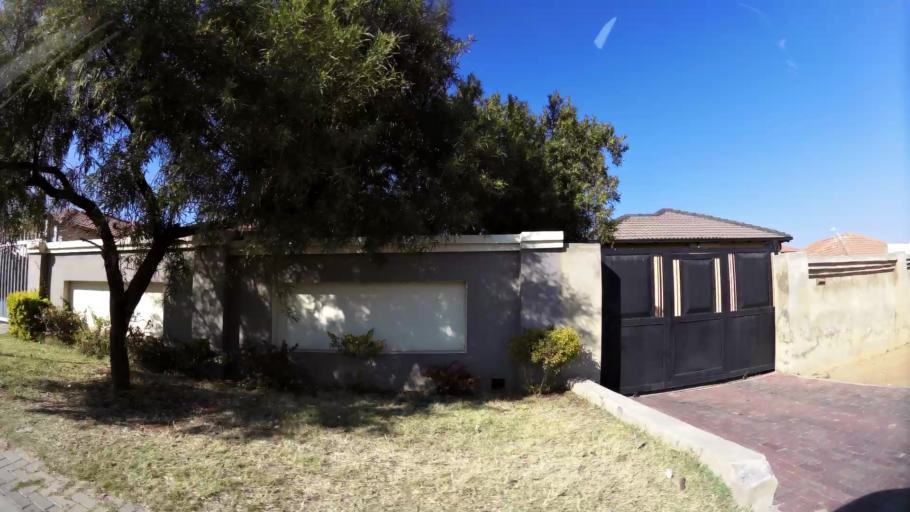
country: ZA
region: Gauteng
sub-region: City of Johannesburg Metropolitan Municipality
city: Modderfontein
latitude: -26.0436
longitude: 28.1965
